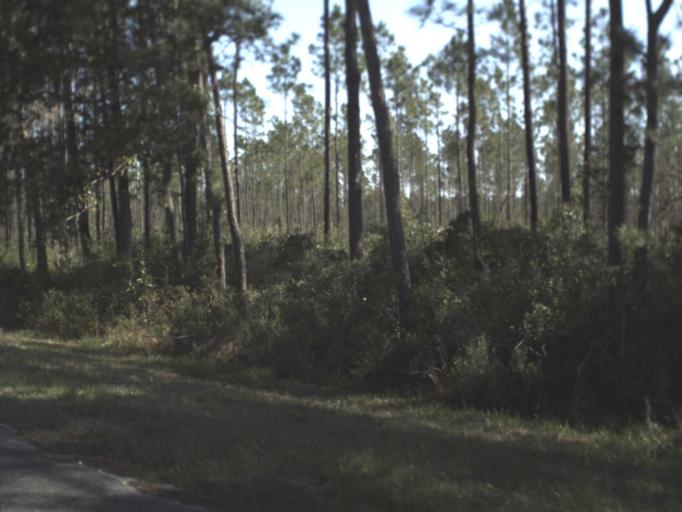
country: US
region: Florida
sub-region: Leon County
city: Woodville
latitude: 30.2390
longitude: -84.0427
